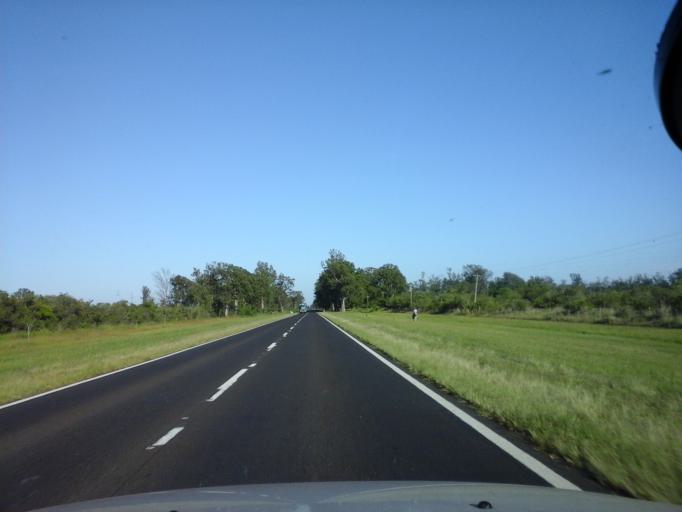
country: AR
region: Corrientes
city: Ita Ibate
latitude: -27.4583
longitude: -57.3193
